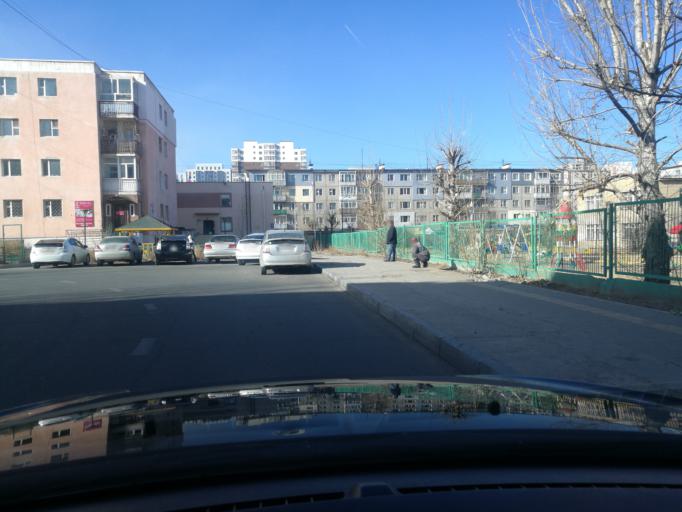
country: MN
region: Ulaanbaatar
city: Ulaanbaatar
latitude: 47.9011
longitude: 106.9042
